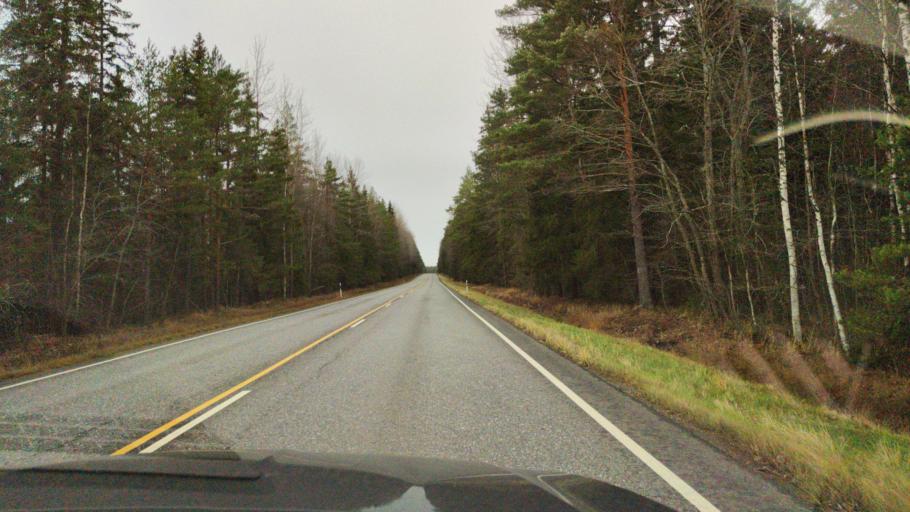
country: FI
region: Varsinais-Suomi
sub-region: Loimaa
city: Ylaene
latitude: 60.7255
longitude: 22.4427
